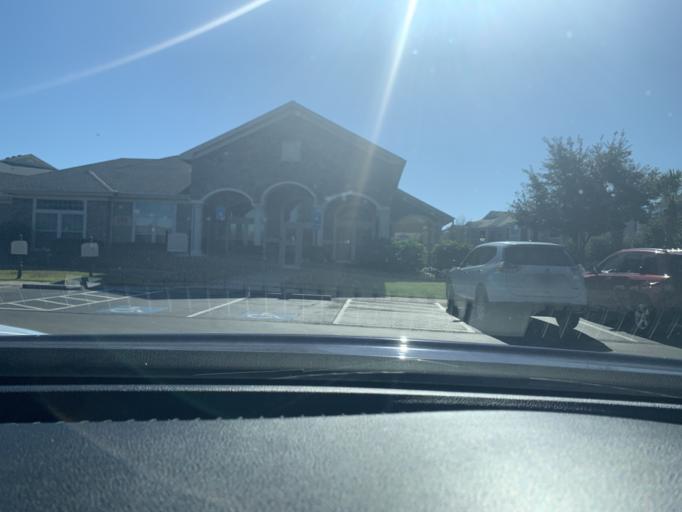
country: US
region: Georgia
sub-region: Chatham County
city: Pooler
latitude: 32.1323
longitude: -81.2506
